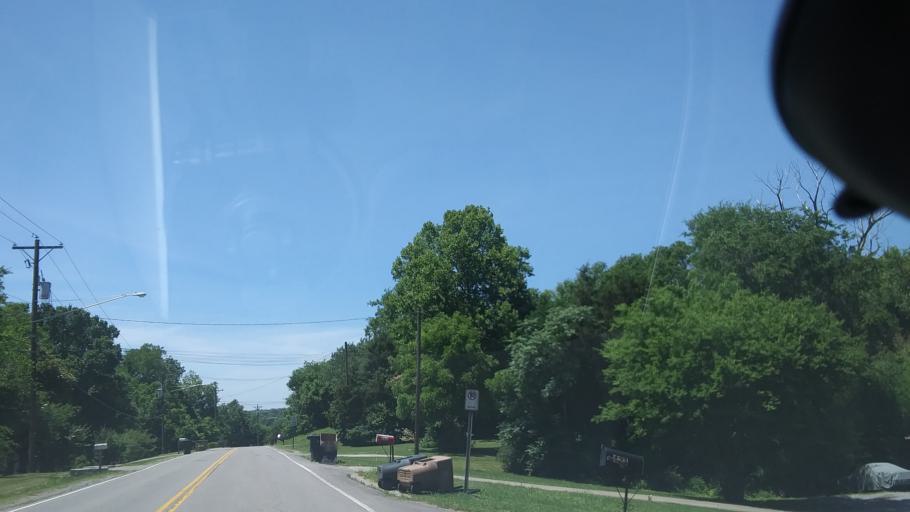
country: US
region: Tennessee
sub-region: Davidson County
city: Oak Hill
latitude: 36.0956
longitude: -86.6743
